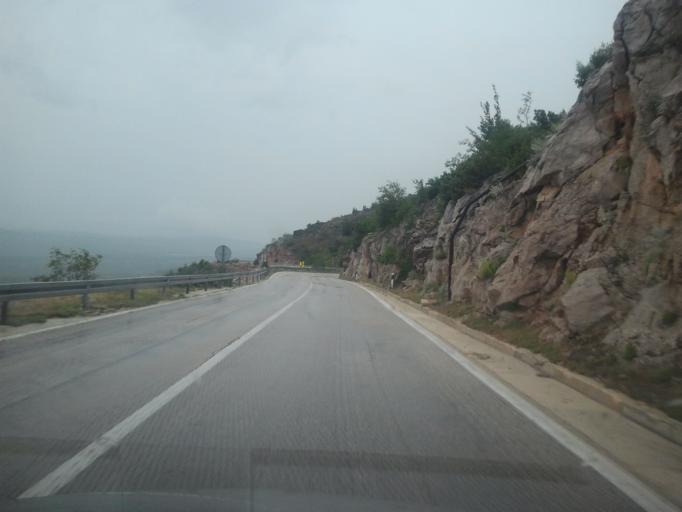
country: HR
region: Zadarska
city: Obrovac
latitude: 44.2228
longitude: 15.7527
